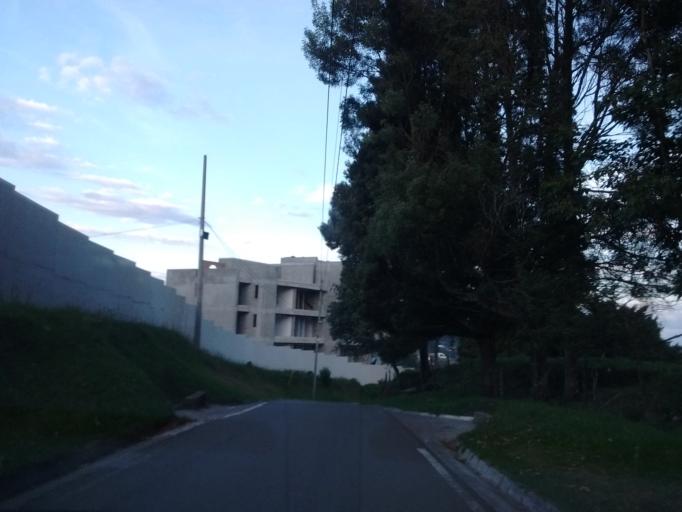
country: CO
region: Antioquia
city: Envigado
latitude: 6.1721
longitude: -75.5014
